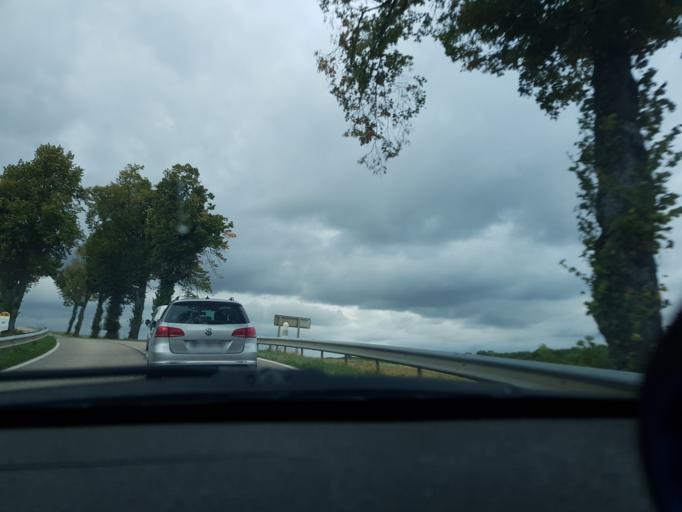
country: FR
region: Lorraine
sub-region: Departement de la Moselle
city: Morhange
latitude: 48.9702
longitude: 6.6101
